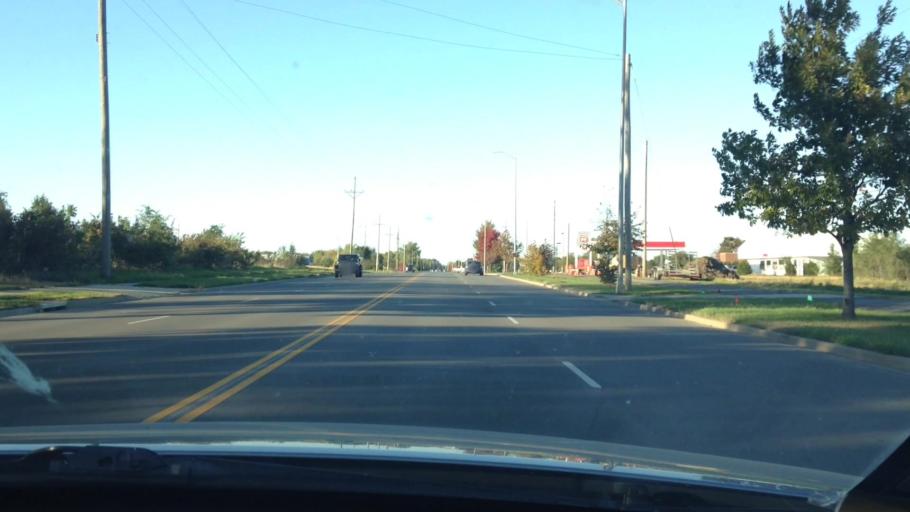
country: US
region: Kansas
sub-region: Johnson County
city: Gardner
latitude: 38.7845
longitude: -94.9274
